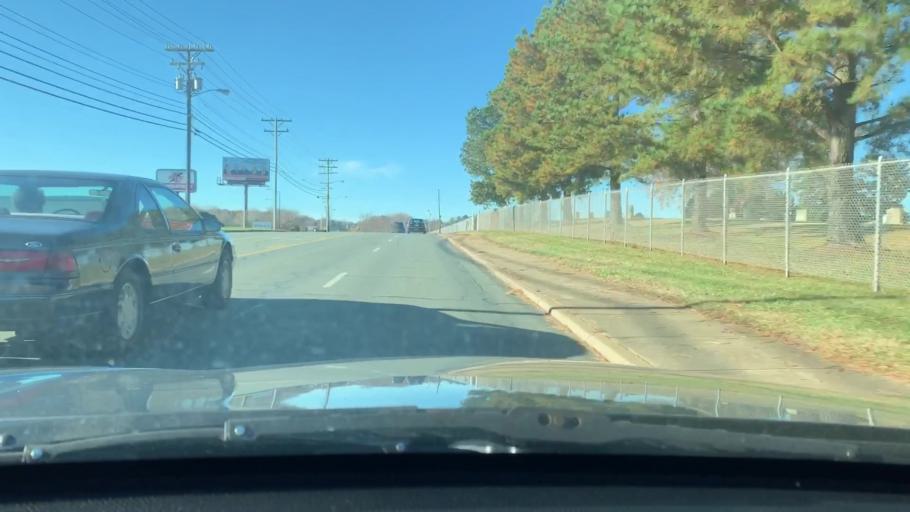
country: US
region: North Carolina
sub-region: Alamance County
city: Burlington
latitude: 36.0828
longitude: -79.4445
